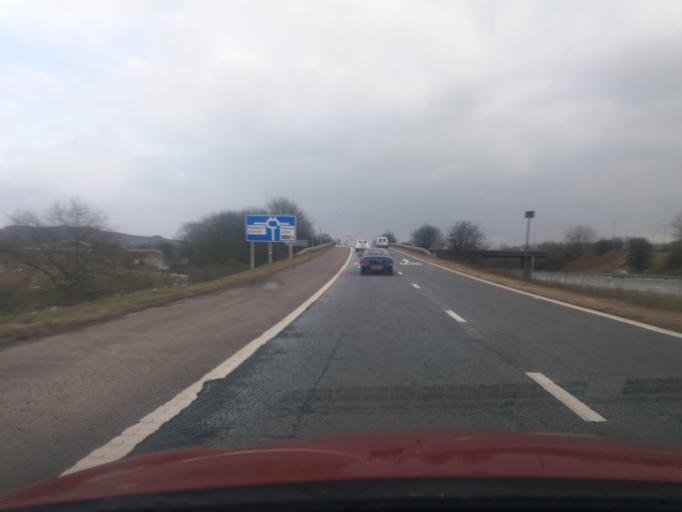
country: GB
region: England
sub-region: Lancashire
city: Chorley
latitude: 53.6724
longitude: -2.6264
